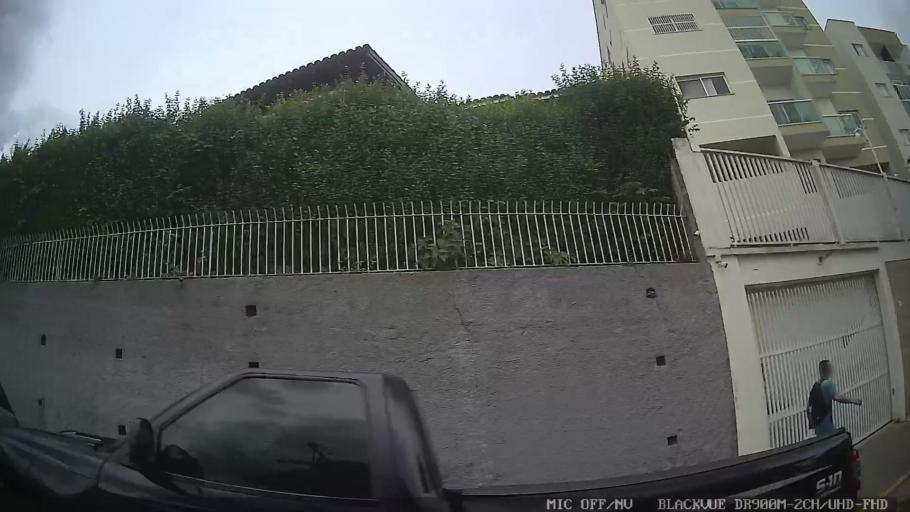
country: BR
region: Sao Paulo
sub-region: Atibaia
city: Atibaia
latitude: -23.1153
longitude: -46.5597
